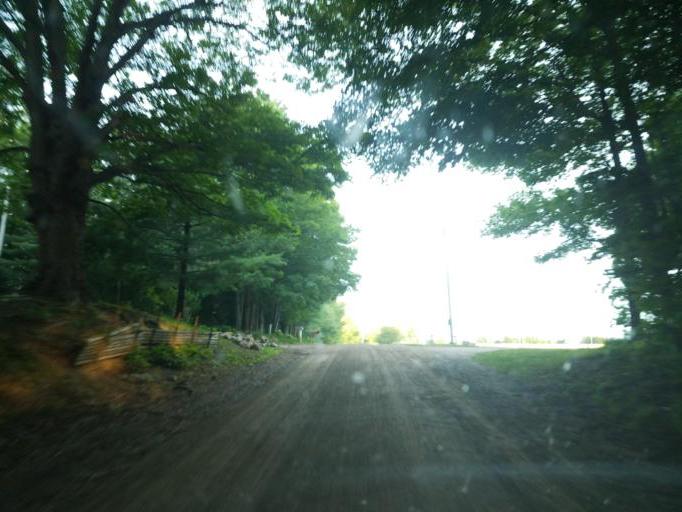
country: US
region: Michigan
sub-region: Barry County
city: Nashville
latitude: 42.5971
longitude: -84.9688
